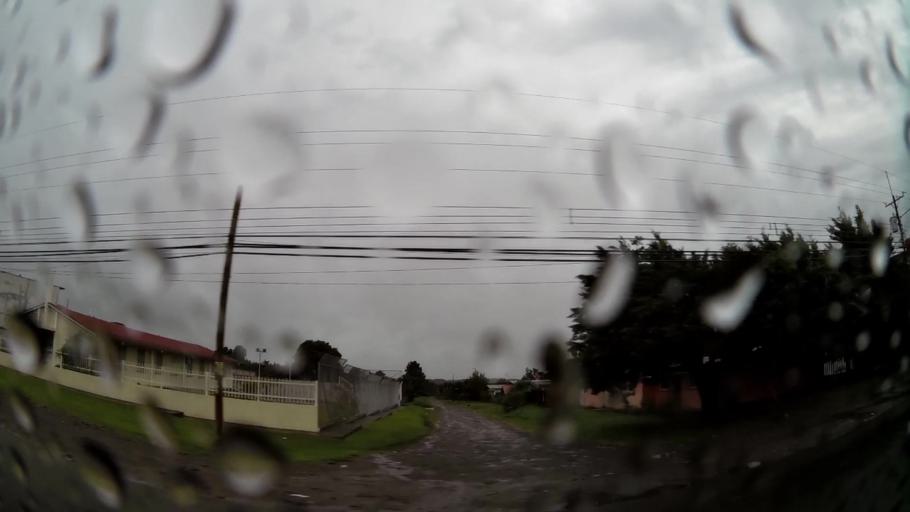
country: PA
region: Chiriqui
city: Volcan
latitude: 8.7782
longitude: -82.6436
